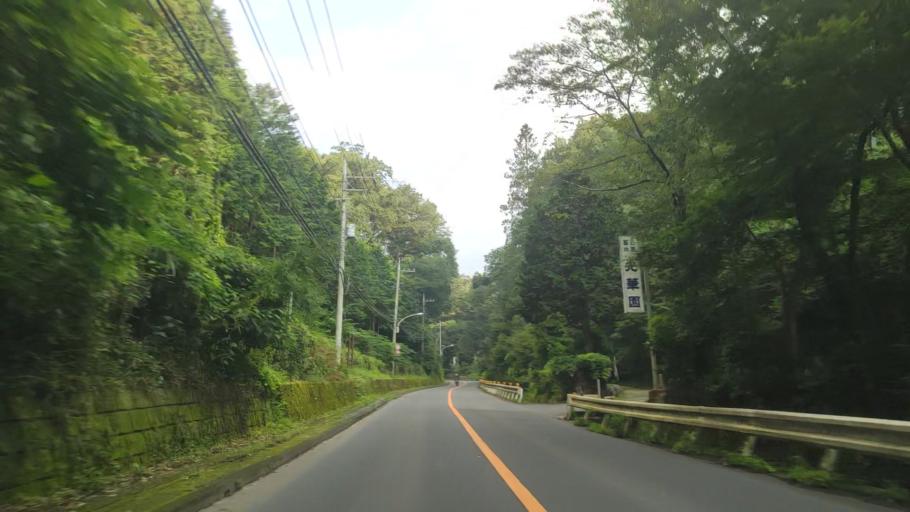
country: JP
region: Saitama
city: Hanno
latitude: 35.8291
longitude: 139.2714
